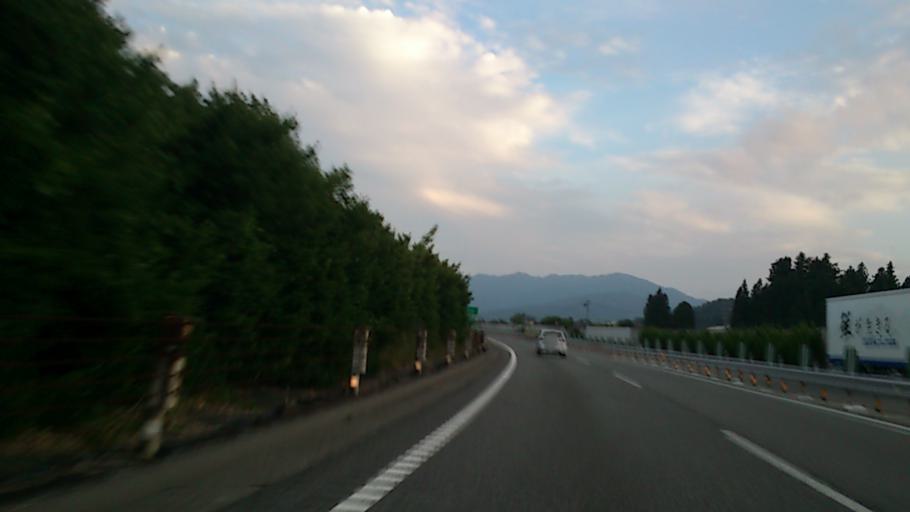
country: JP
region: Nagano
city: Iida
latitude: 35.4784
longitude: 137.7611
